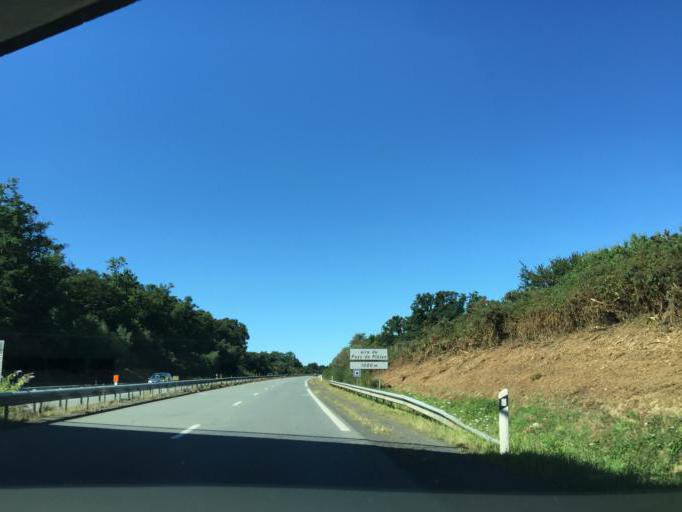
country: FR
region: Brittany
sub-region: Departement des Cotes-d'Armor
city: Trelivan
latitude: 48.4307
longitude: -2.1612
